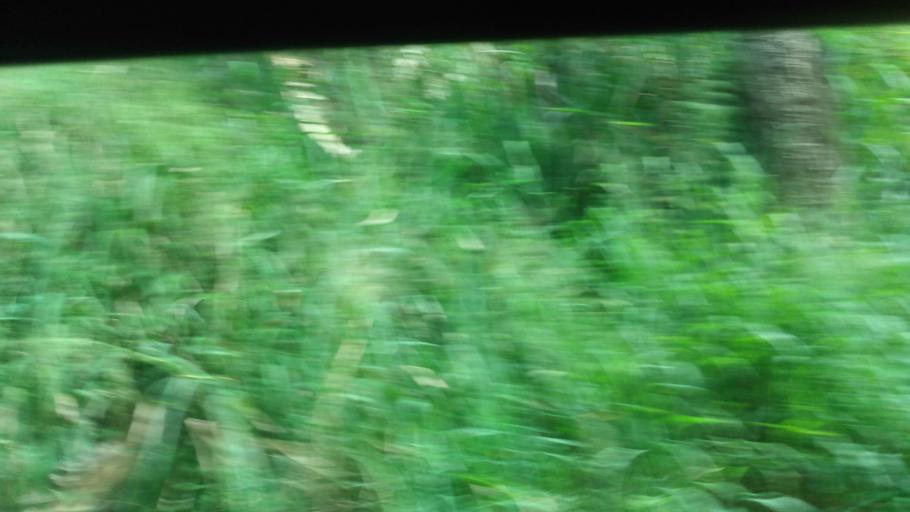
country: BR
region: Pernambuco
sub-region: Maraial
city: Maraial
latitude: -8.7897
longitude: -35.8945
